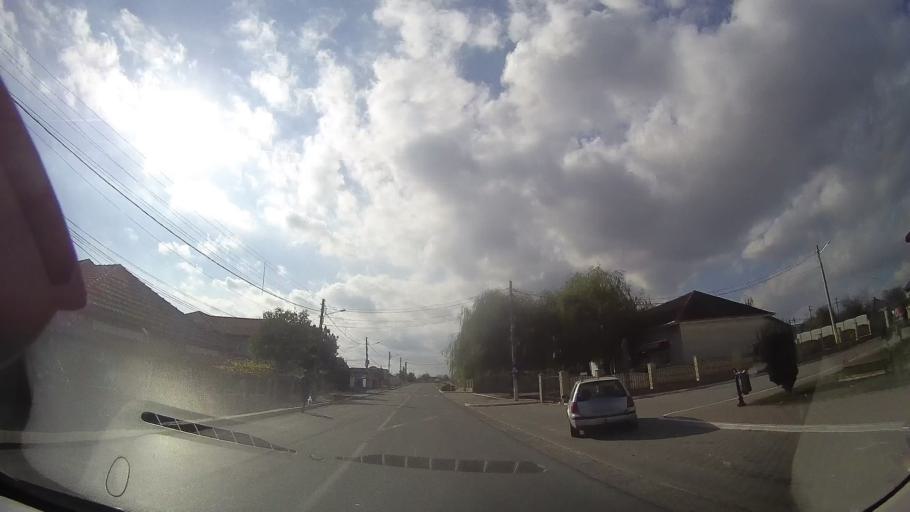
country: RO
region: Constanta
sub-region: Comuna Douazeci si Trei August
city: Dulcesti
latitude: 43.9057
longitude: 28.5460
